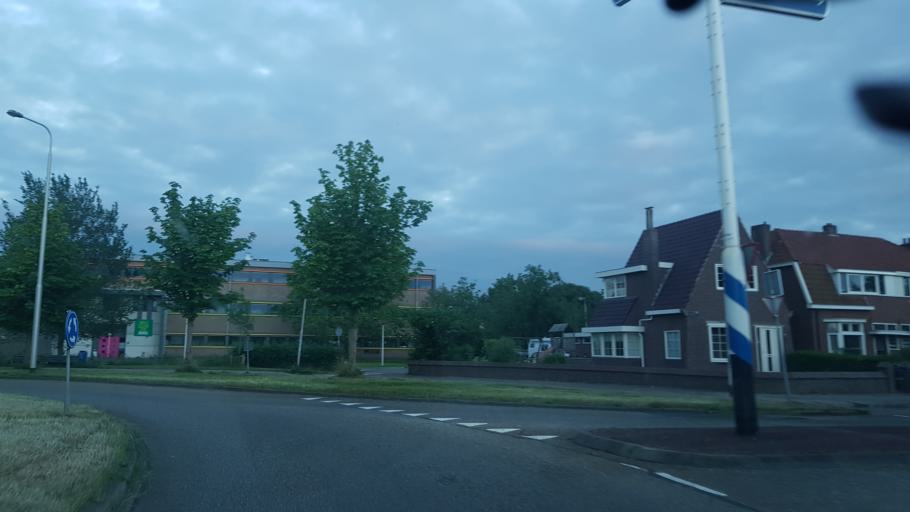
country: NL
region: Friesland
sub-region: Gemeente Leeuwarden
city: Leeuwarden
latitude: 53.2121
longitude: 5.8137
